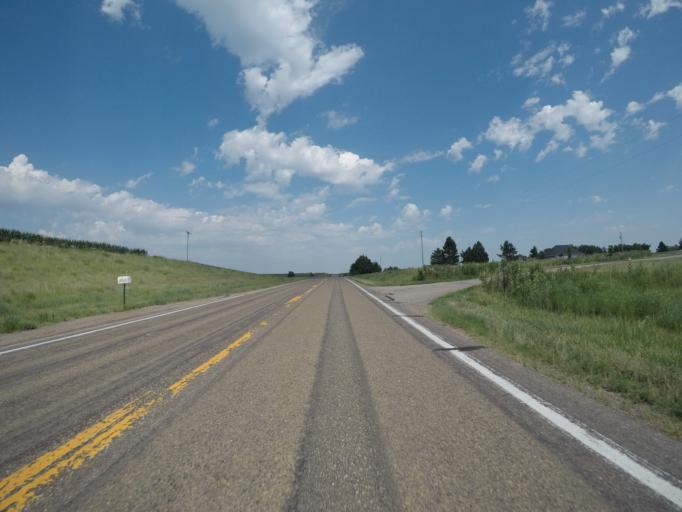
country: US
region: Nebraska
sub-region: Nuckolls County
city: Superior
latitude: 40.0165
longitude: -97.8977
